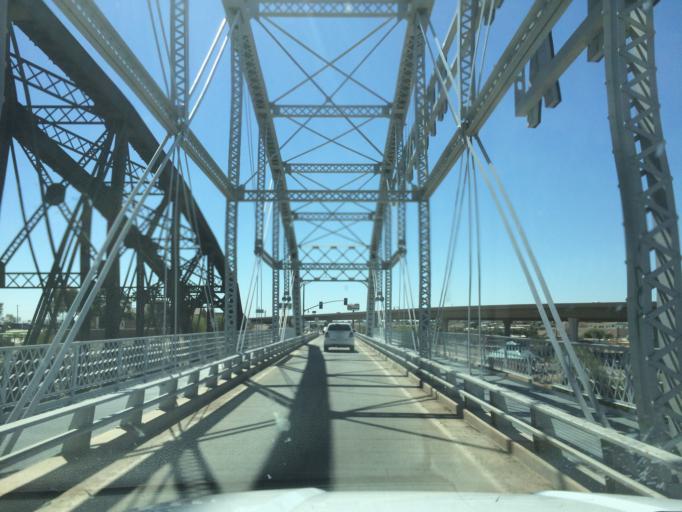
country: US
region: Arizona
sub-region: Yuma County
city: Yuma
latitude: 32.7286
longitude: -114.6156
